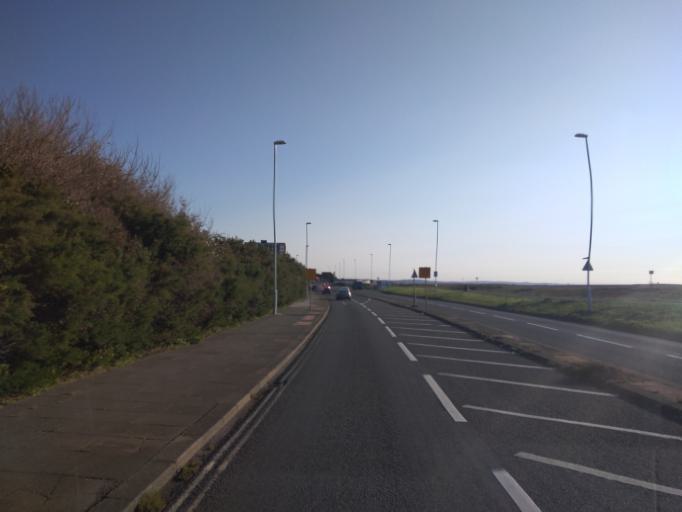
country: GB
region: England
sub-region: West Sussex
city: Lancing
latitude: 50.8168
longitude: -0.3363
